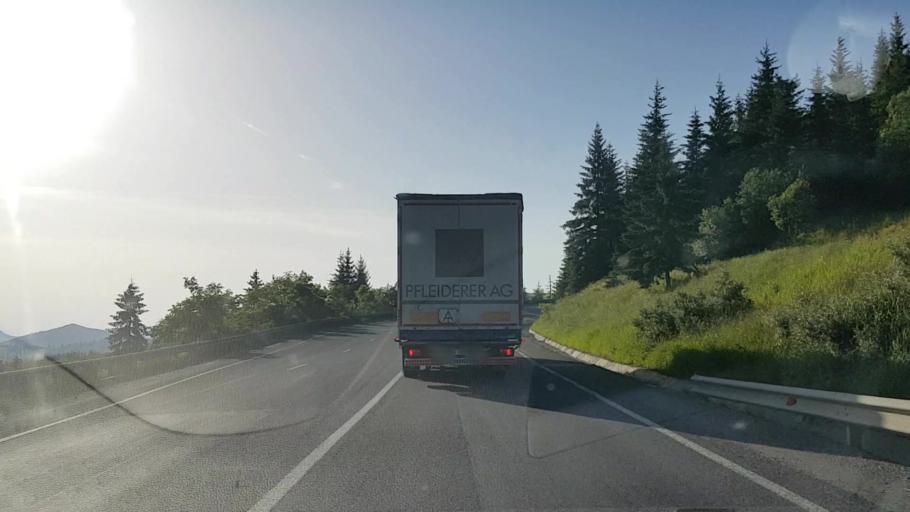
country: RO
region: Bistrita-Nasaud
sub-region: Comuna Lunca Ilvei
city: Lunca Ilvei
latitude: 47.2637
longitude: 25.0209
